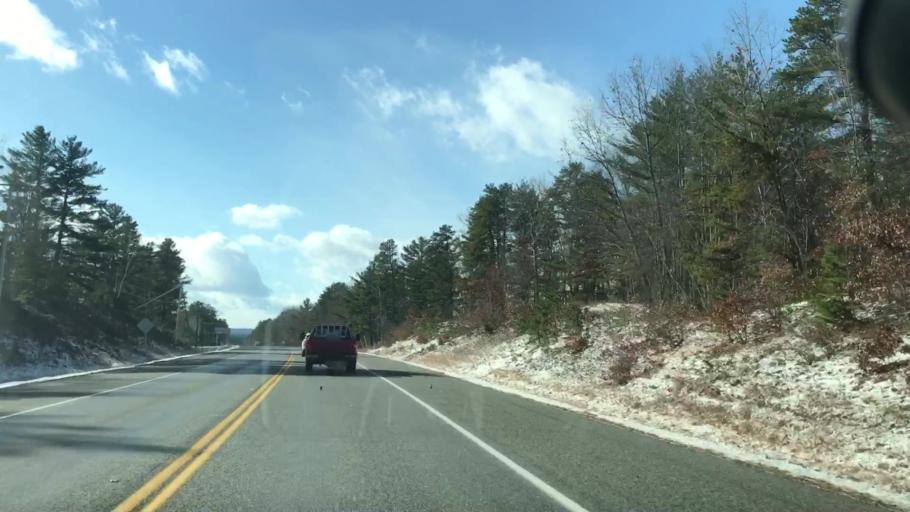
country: US
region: New Hampshire
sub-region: Carroll County
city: Freedom
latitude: 43.7819
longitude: -71.1018
